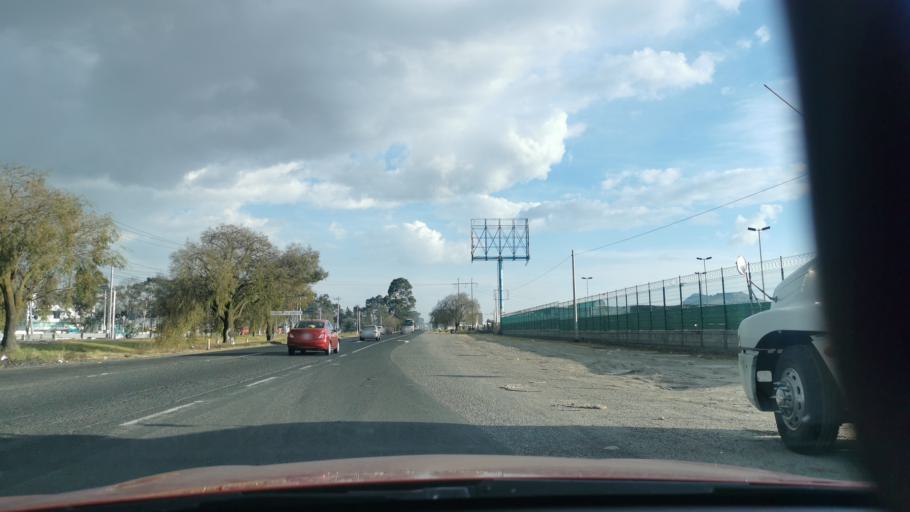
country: MX
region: Mexico
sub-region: Toluca
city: Colonia Aviacion Autopan
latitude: 19.3813
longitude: -99.7050
